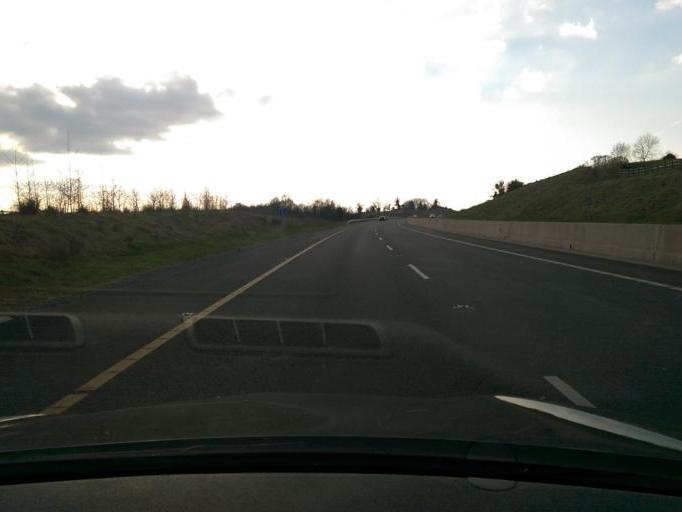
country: IE
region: Munster
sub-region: North Tipperary
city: Roscrea
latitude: 52.9147
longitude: -7.7047
